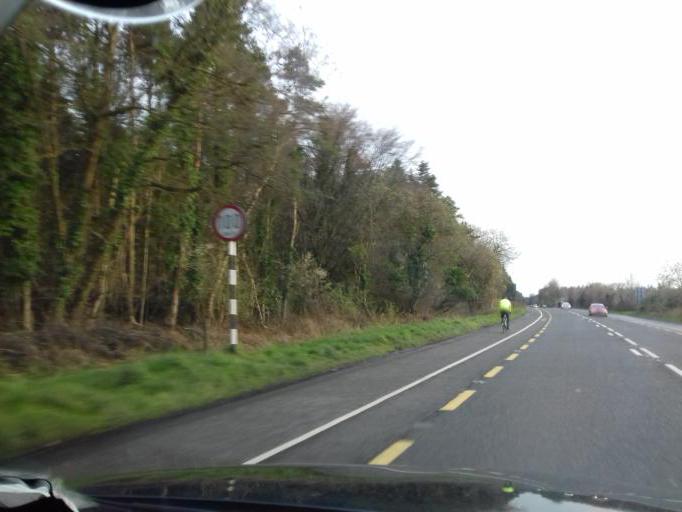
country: IE
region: Leinster
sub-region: Laois
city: Abbeyleix
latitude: 52.9006
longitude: -7.3573
